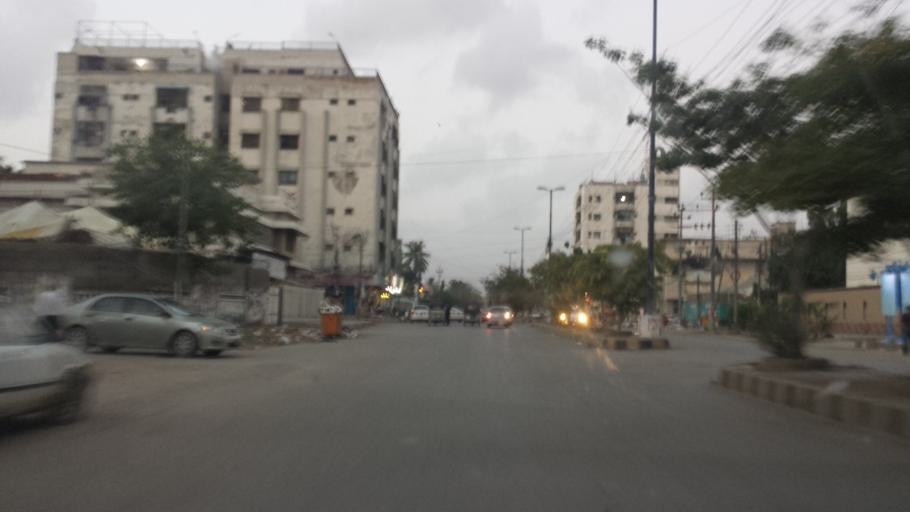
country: PK
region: Sindh
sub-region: Karachi District
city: Karachi
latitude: 24.8839
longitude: 67.0684
